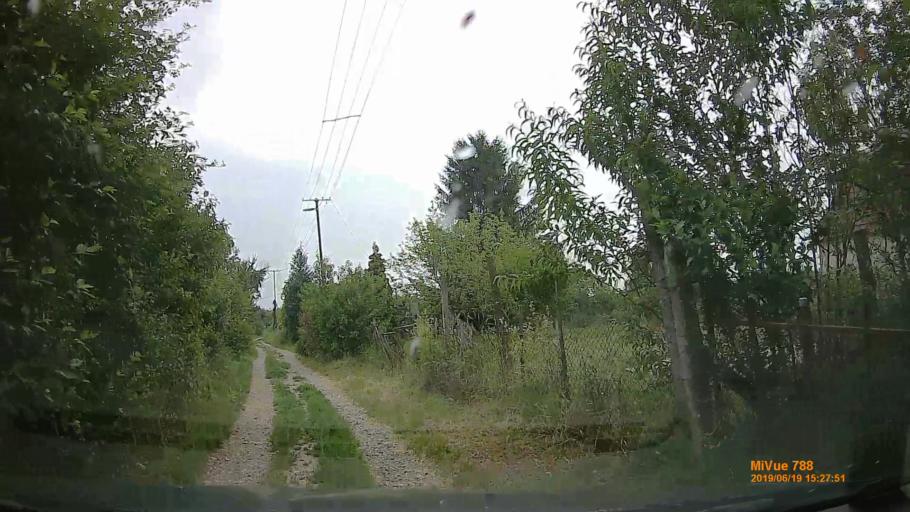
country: HU
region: Baranya
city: Szigetvar
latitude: 46.0727
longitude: 17.8469
